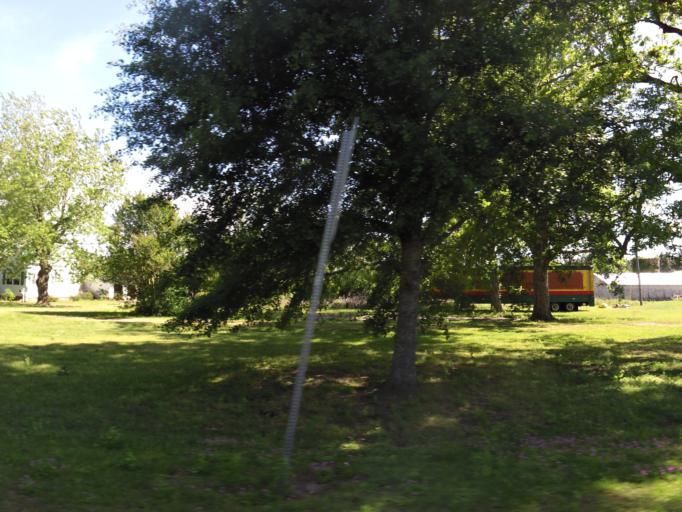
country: US
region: South Carolina
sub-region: Barnwell County
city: Blackville
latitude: 33.3482
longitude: -81.2133
